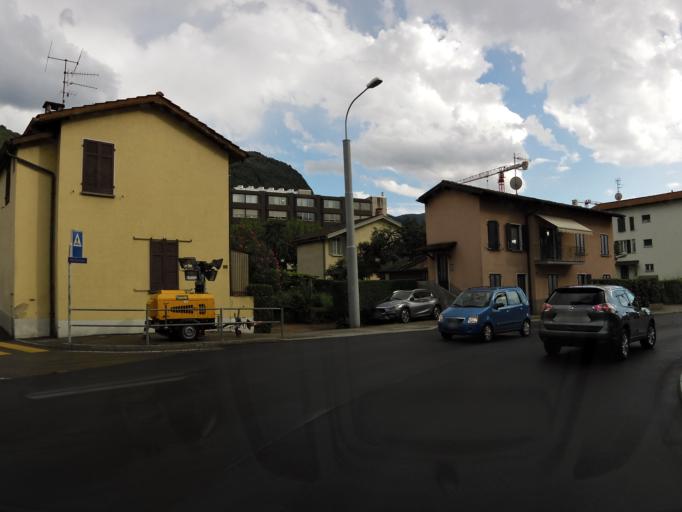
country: CH
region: Ticino
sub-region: Lugano District
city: Pregassona
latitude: 46.0235
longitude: 8.9680
